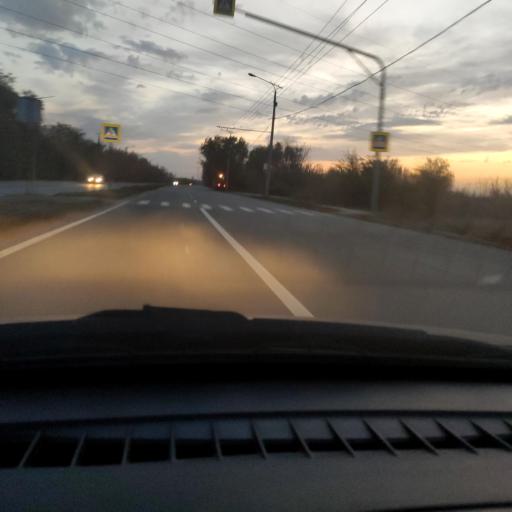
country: RU
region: Samara
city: Zhigulevsk
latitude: 53.5452
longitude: 49.5844
